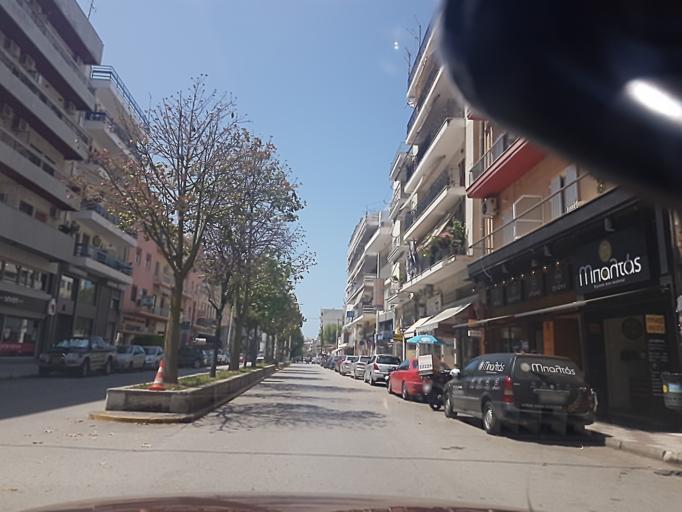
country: GR
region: Central Greece
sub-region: Nomos Evvoias
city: Chalkida
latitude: 38.4610
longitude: 23.5963
